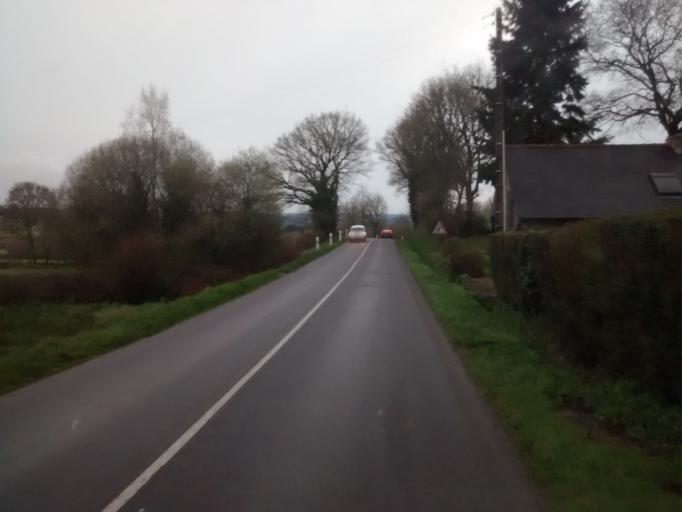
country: FR
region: Brittany
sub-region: Departement du Morbihan
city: Malestroit
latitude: 47.8228
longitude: -2.4287
